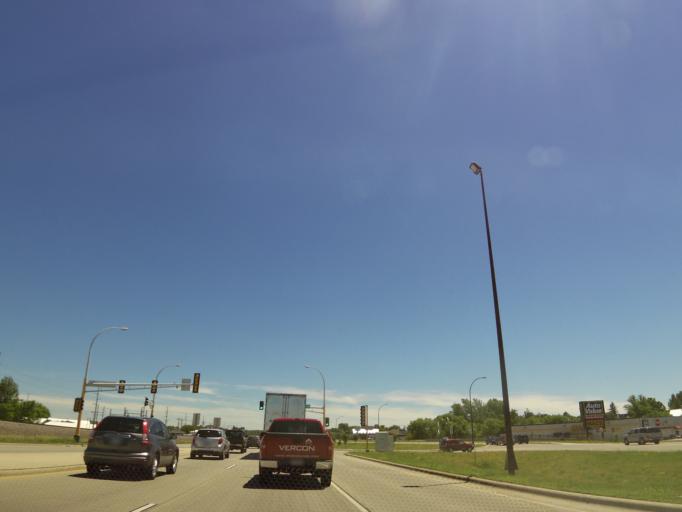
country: US
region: Minnesota
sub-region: Becker County
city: Detroit Lakes
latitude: 46.8146
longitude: -95.8346
